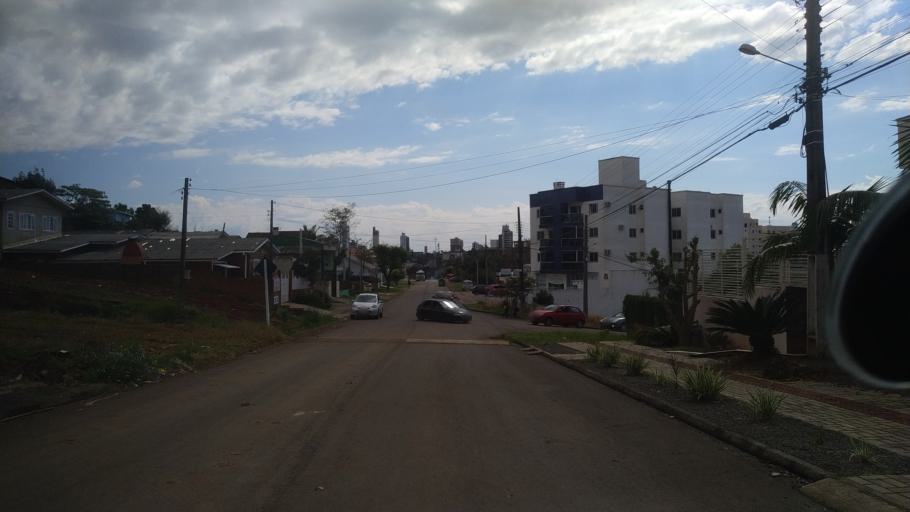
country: BR
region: Santa Catarina
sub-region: Chapeco
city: Chapeco
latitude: -27.1150
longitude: -52.6034
